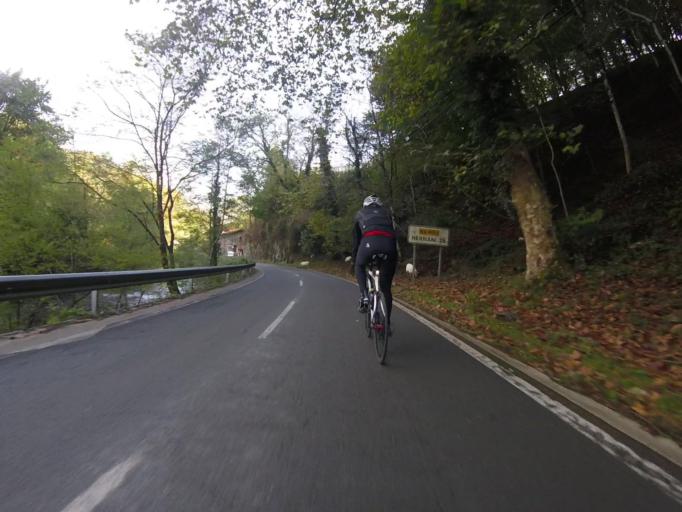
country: ES
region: Navarre
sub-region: Provincia de Navarra
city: Goizueta
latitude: 43.1765
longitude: -1.8615
